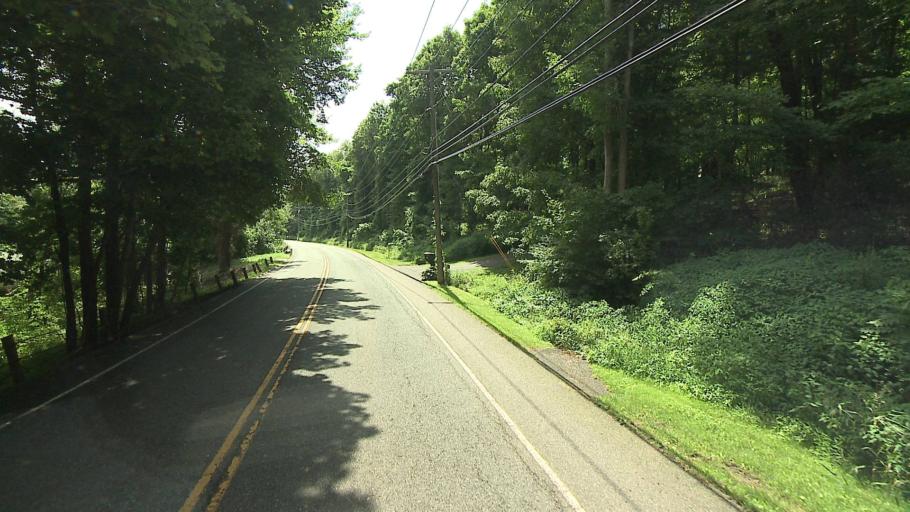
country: US
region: Connecticut
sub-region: Fairfield County
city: Sherman
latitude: 41.5556
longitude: -73.4887
